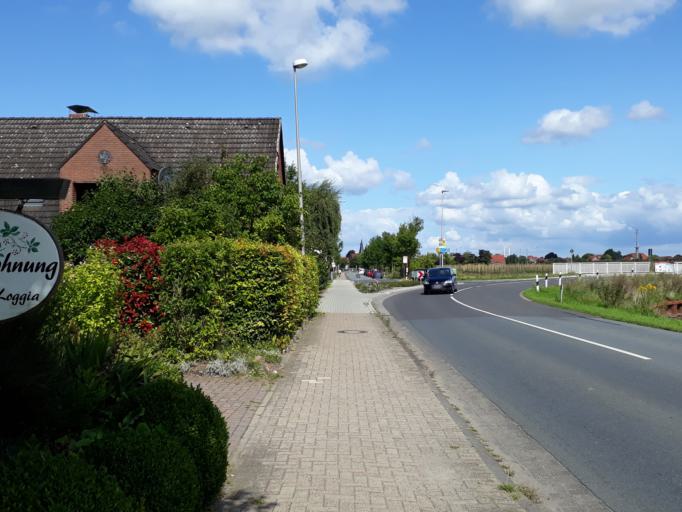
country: DE
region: Lower Saxony
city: Jork
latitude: 53.5255
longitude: 9.6759
